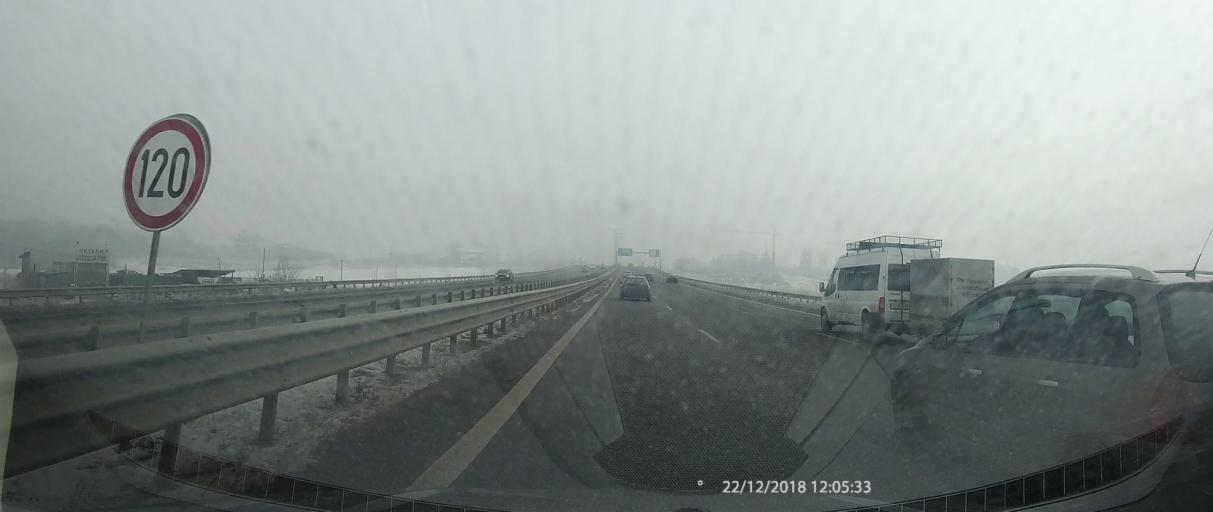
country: BG
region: Sofia-Capital
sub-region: Stolichna Obshtina
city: Sofia
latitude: 42.7599
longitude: 23.3139
